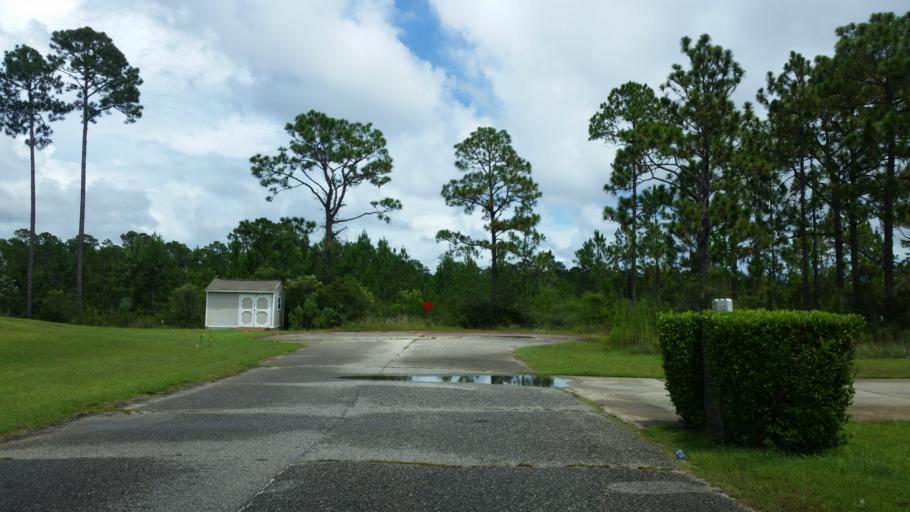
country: US
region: Florida
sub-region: Santa Rosa County
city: Navarre
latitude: 30.4304
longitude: -86.8509
